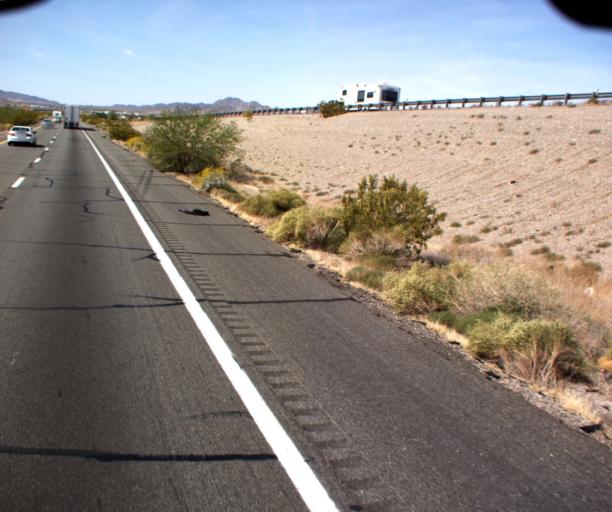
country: US
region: Arizona
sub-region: La Paz County
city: Quartzsite
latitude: 33.6656
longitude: -114.2009
